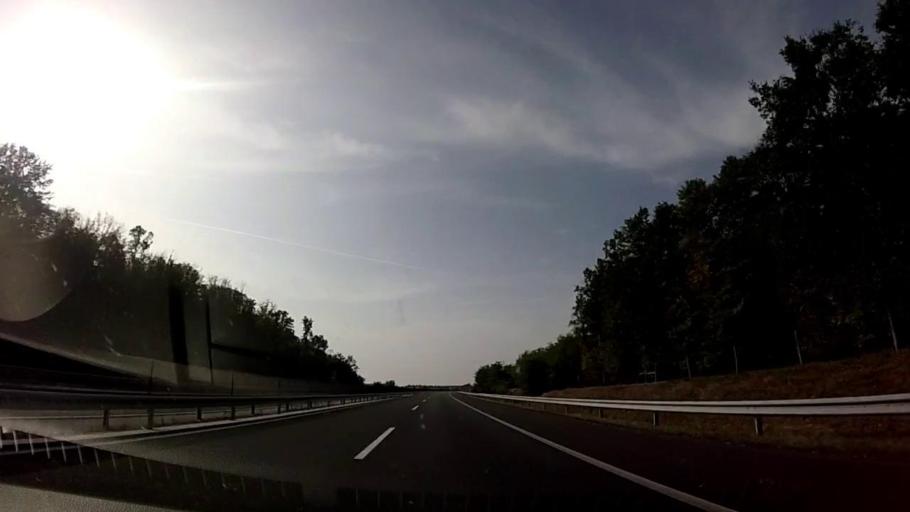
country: HU
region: Somogy
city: Balatonbereny
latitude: 46.6334
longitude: 17.2811
